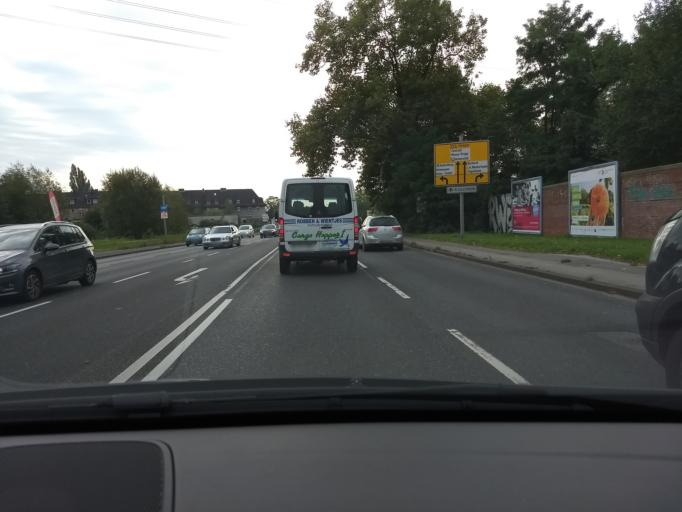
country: DE
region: North Rhine-Westphalia
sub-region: Regierungsbezirk Dusseldorf
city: Essen
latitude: 51.4944
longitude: 6.9969
